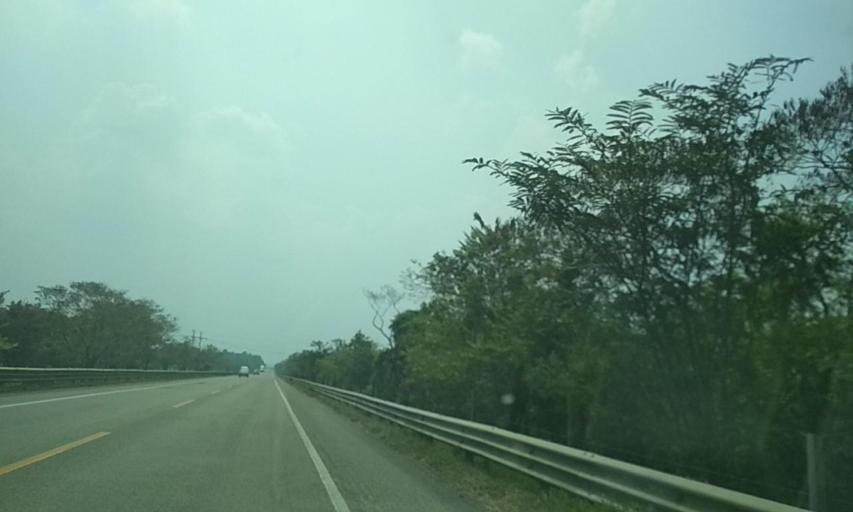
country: MX
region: Tabasco
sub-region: Huimanguillo
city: Francisco Rueda
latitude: 17.7633
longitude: -94.0164
